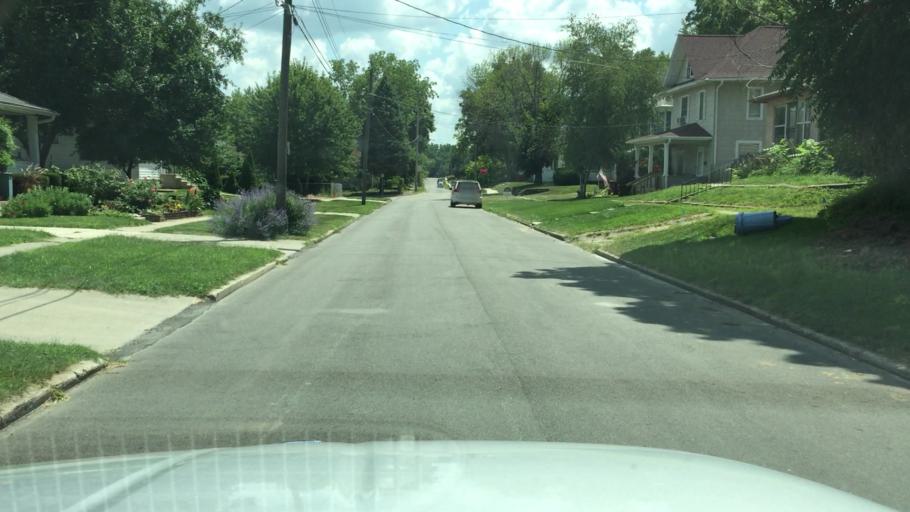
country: US
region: Iowa
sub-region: Jasper County
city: Newton
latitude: 41.6965
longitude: -93.0549
